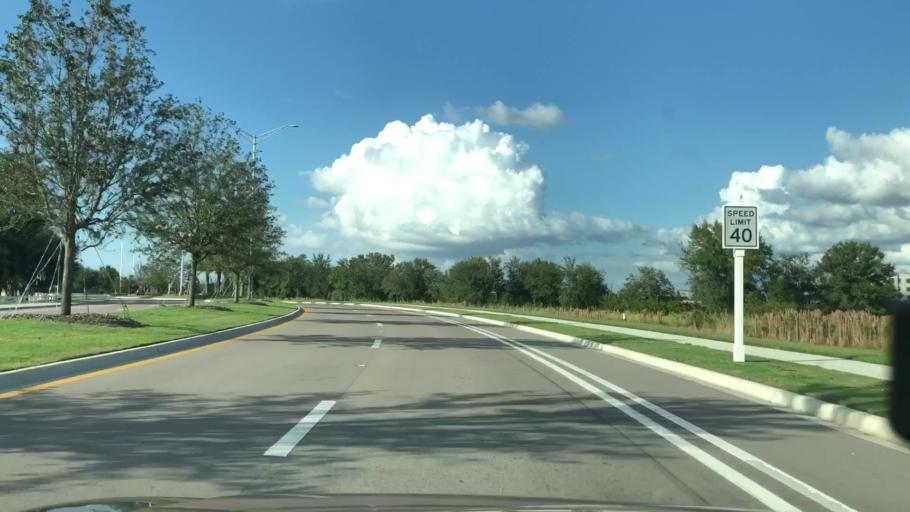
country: US
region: Florida
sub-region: Sarasota County
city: The Meadows
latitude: 27.3818
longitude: -82.3962
